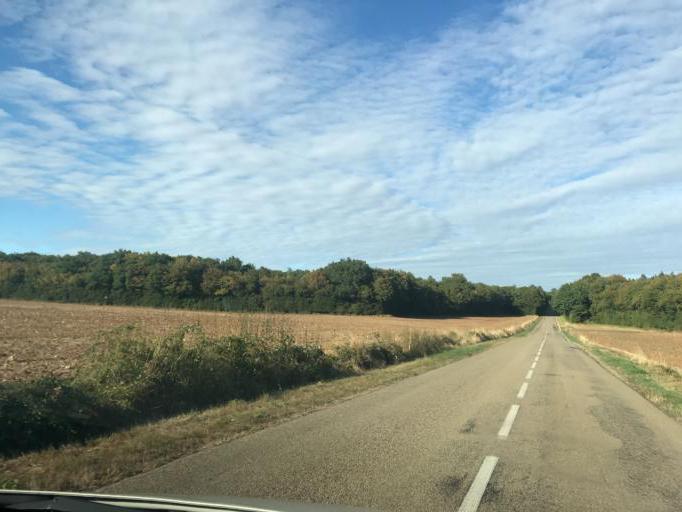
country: FR
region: Bourgogne
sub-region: Departement de l'Yonne
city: Fontenailles
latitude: 47.5651
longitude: 3.4436
